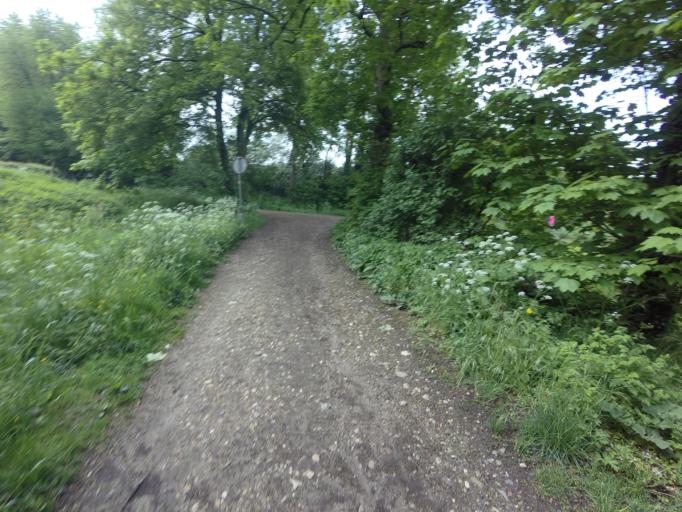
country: NL
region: Limburg
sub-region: Valkenburg aan de Geul
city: Berg
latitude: 50.8411
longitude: 5.7697
